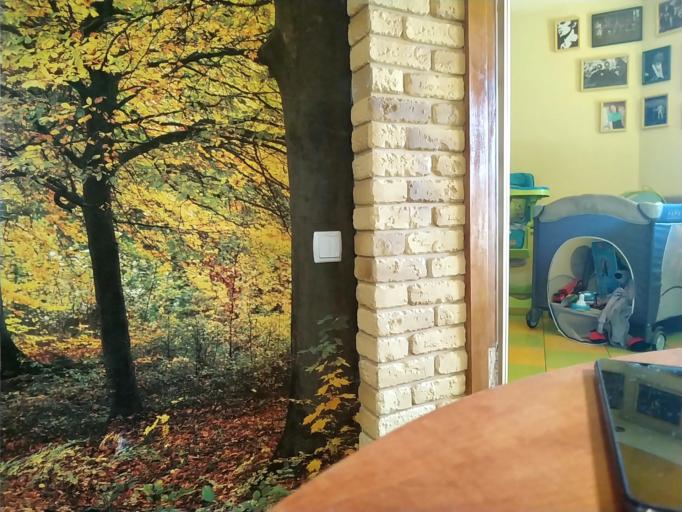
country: RU
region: Tverskaya
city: Krasnomayskiy
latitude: 57.5290
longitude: 34.1685
